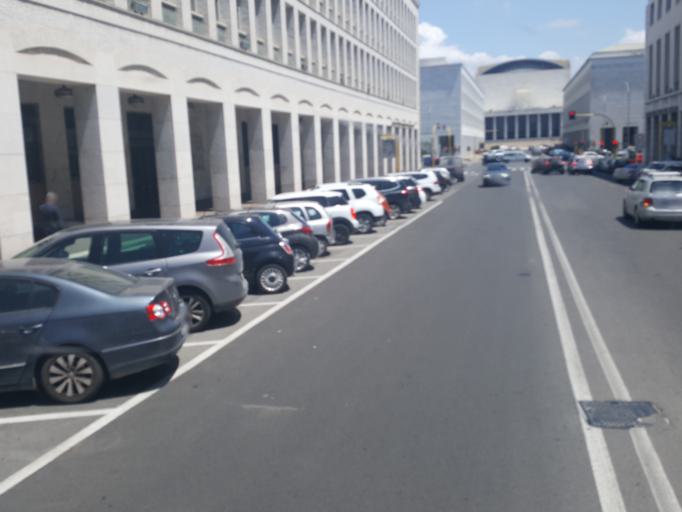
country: VA
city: Vatican City
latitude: 41.8352
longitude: 12.4700
